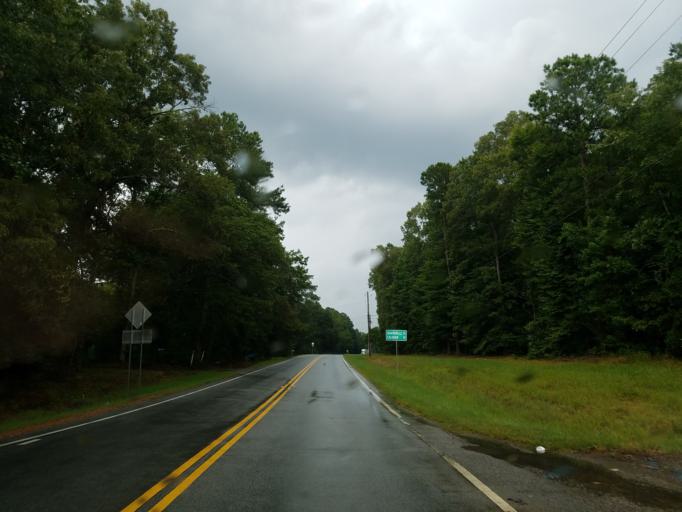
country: US
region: Georgia
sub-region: Floyd County
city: Shannon
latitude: 34.3859
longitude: -85.1767
